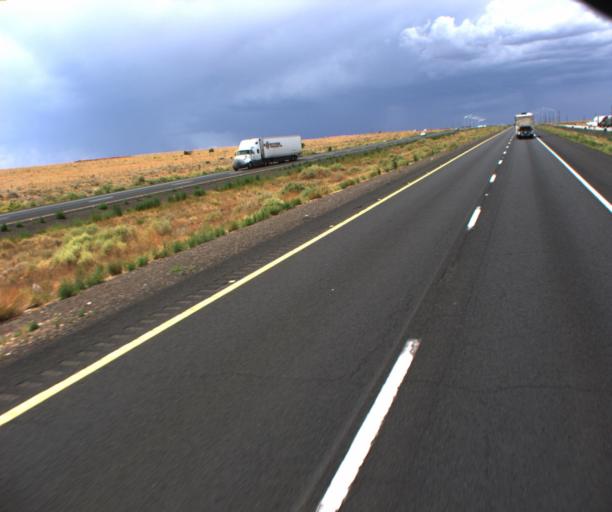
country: US
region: Arizona
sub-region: Coconino County
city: LeChee
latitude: 35.1028
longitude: -110.9910
